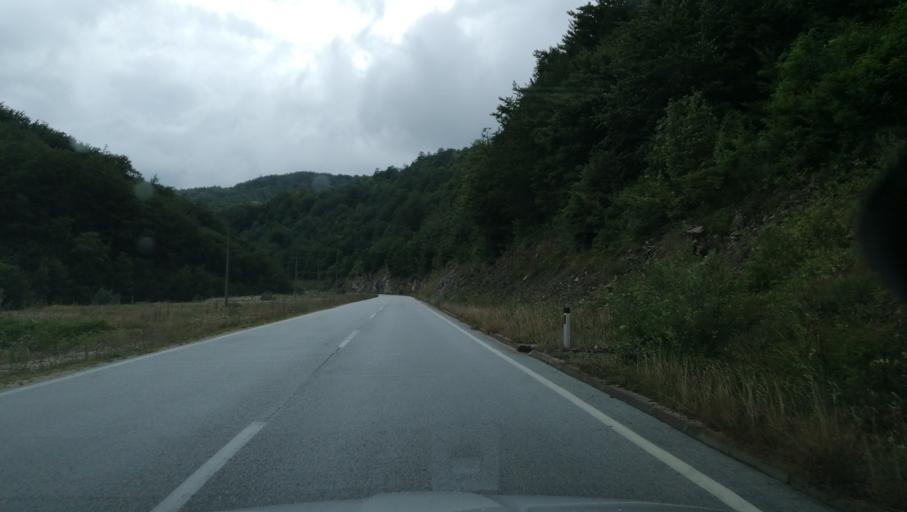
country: BA
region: Republika Srpska
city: Gacko
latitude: 43.2324
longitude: 18.5900
